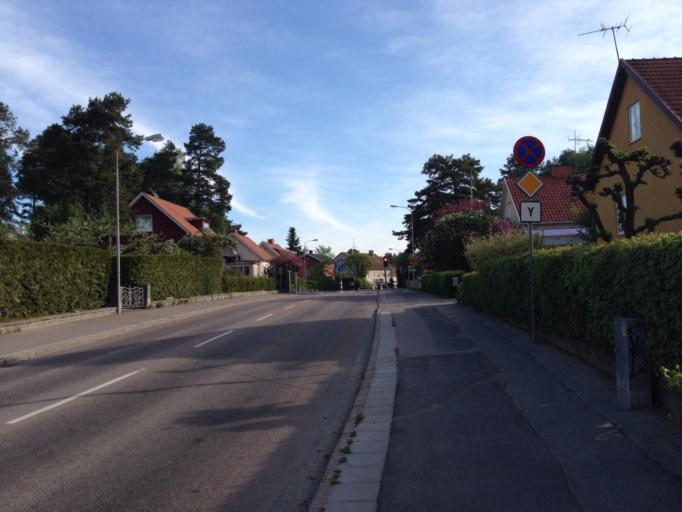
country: SE
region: OEstergoetland
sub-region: Linkopings Kommun
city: Linkoping
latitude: 58.3942
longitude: 15.6473
